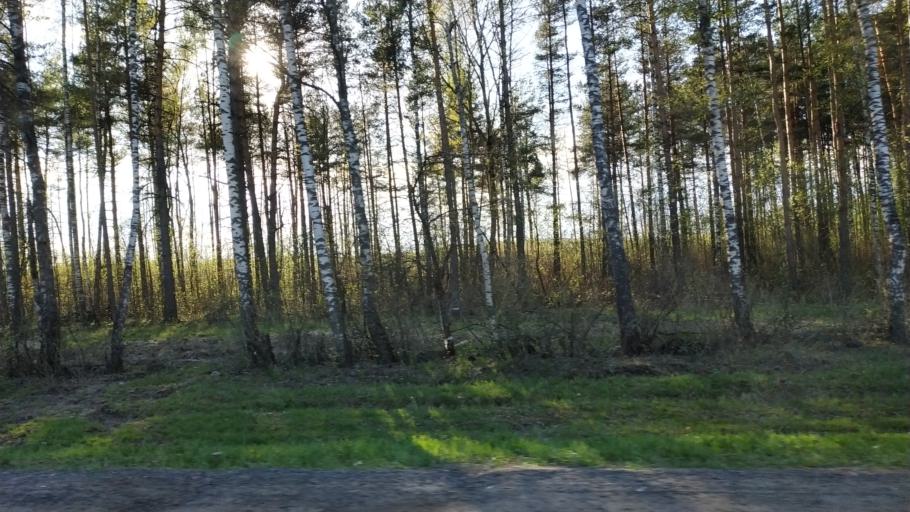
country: RU
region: Moskovskaya
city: Gzhel'
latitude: 55.6392
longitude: 38.3664
